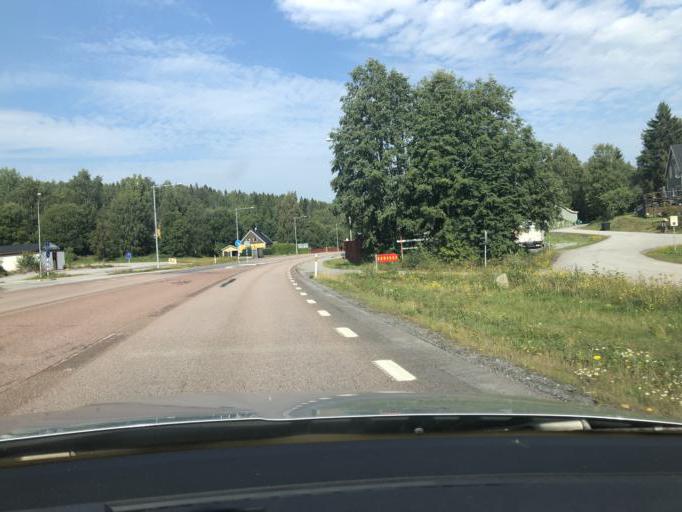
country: SE
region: Vaesternorrland
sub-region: Kramfors Kommun
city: Kramfors
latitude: 62.8041
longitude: 17.8670
